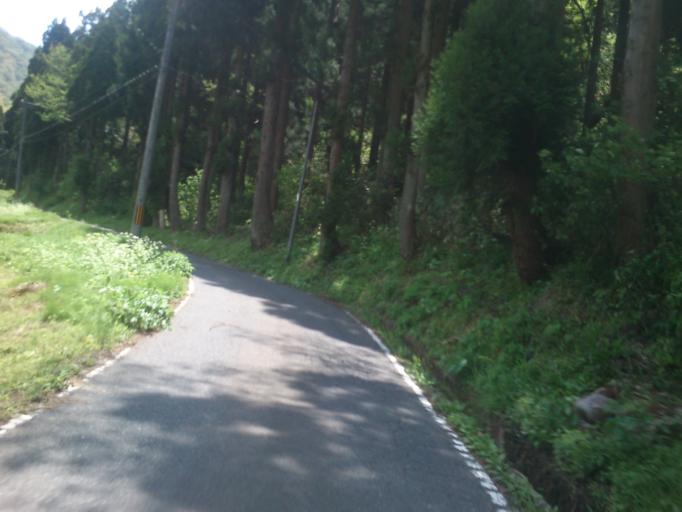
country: JP
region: Kyoto
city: Miyazu
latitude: 35.6624
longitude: 135.1596
